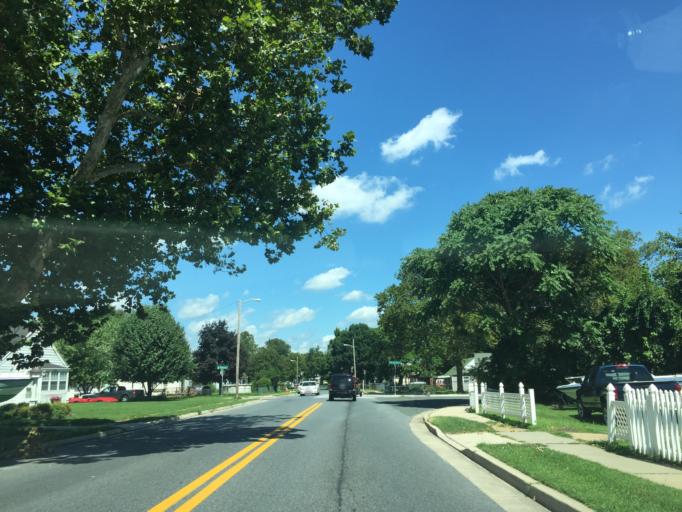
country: US
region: Maryland
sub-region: Baltimore County
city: Dundalk
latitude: 39.2464
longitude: -76.5079
